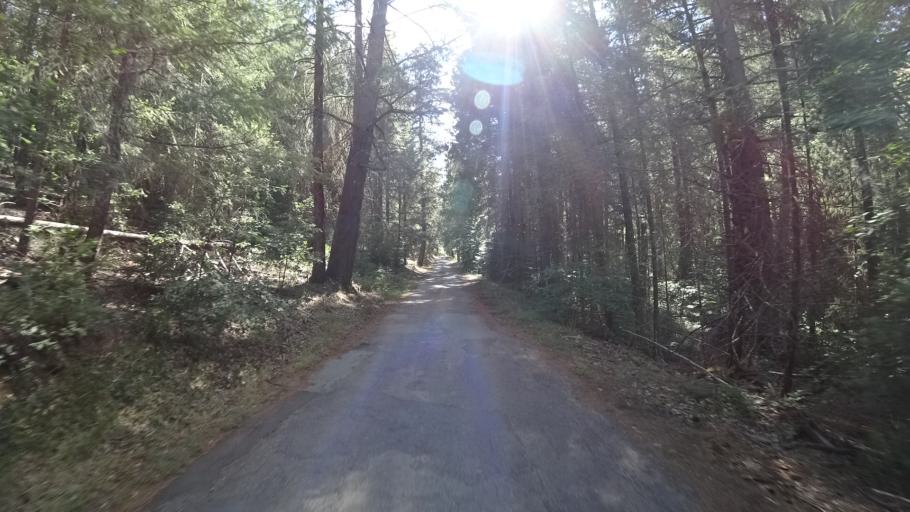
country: US
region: California
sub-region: Amador County
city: Pioneer
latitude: 38.3688
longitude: -120.4484
